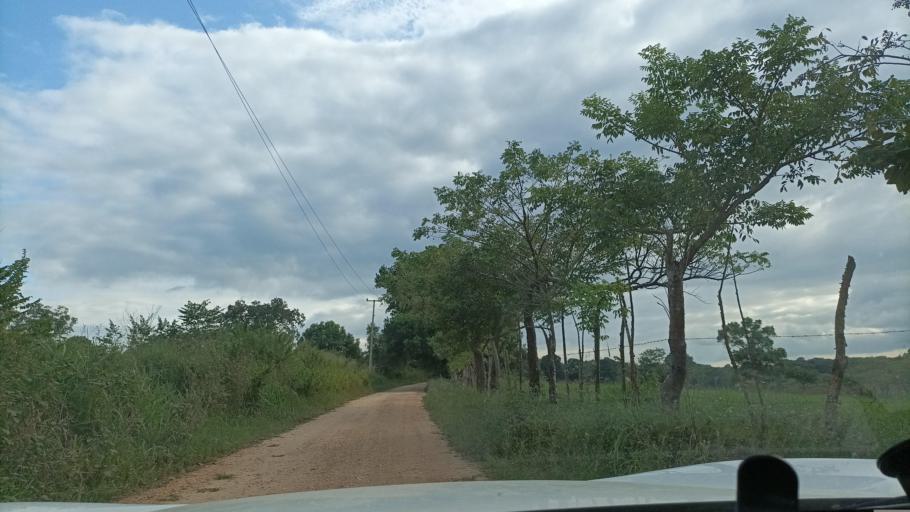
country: MX
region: Veracruz
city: Oluta
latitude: 17.9381
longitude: -94.8820
